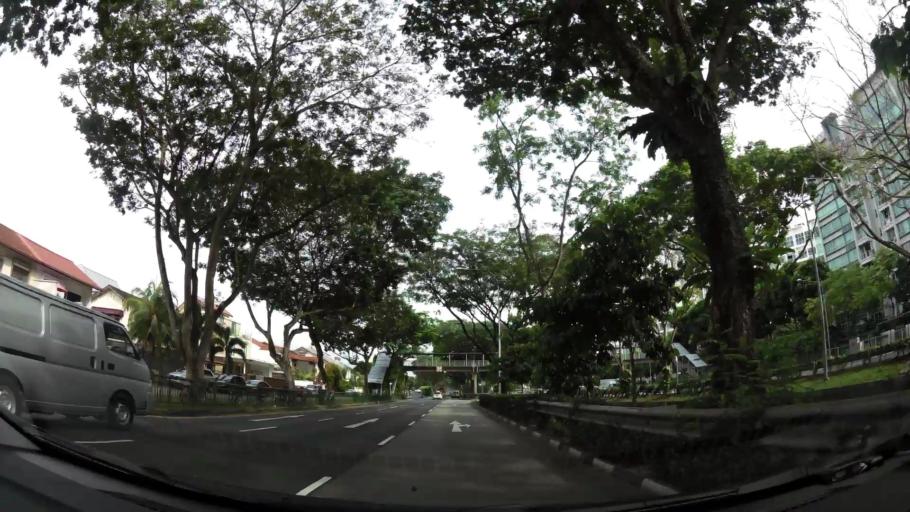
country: SG
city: Singapore
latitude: 1.3349
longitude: 103.7869
